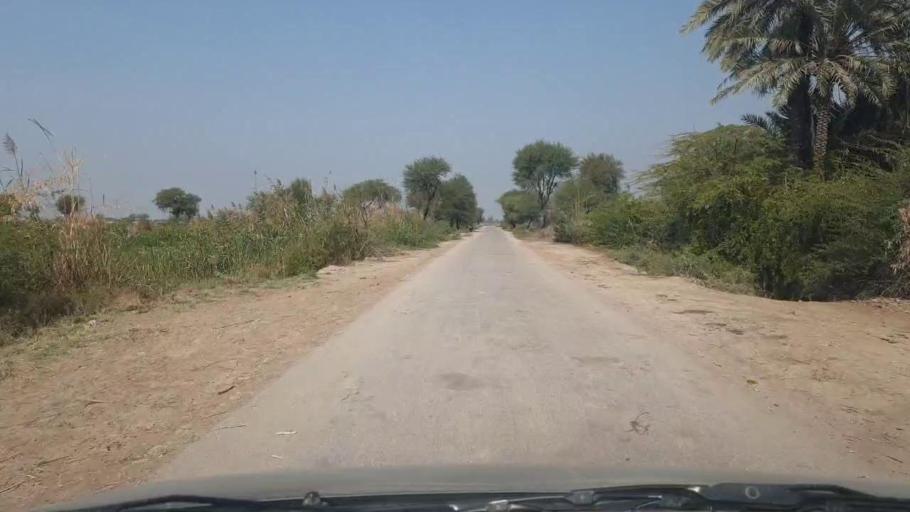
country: PK
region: Sindh
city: Mirwah Gorchani
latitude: 25.3298
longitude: 69.1480
